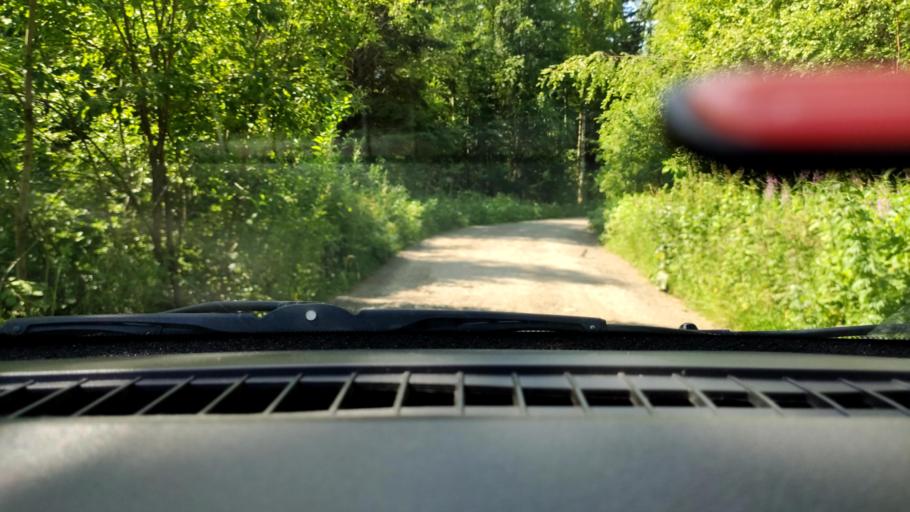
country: RU
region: Perm
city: Perm
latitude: 58.1473
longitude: 56.2951
